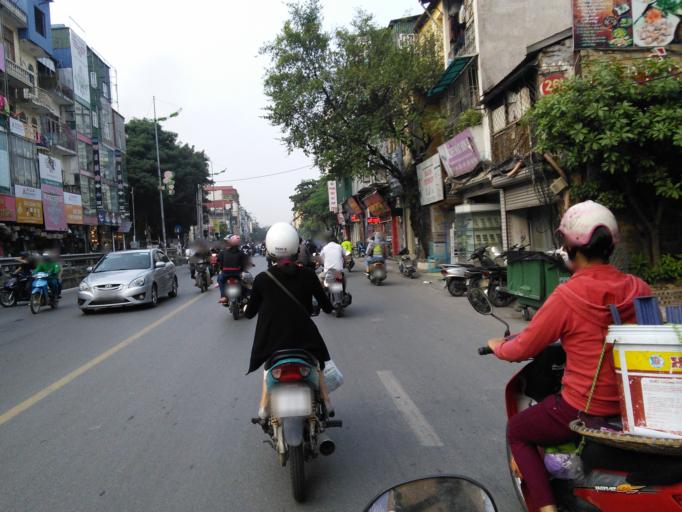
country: VN
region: Ha Noi
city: Hai BaTrung
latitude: 21.0156
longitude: 105.8414
